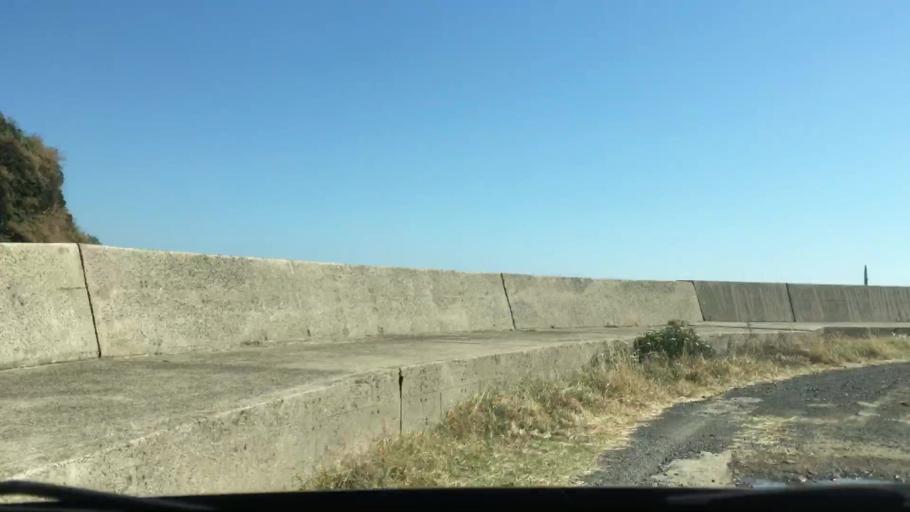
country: JP
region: Nagasaki
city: Sasebo
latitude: 33.0018
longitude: 129.5542
